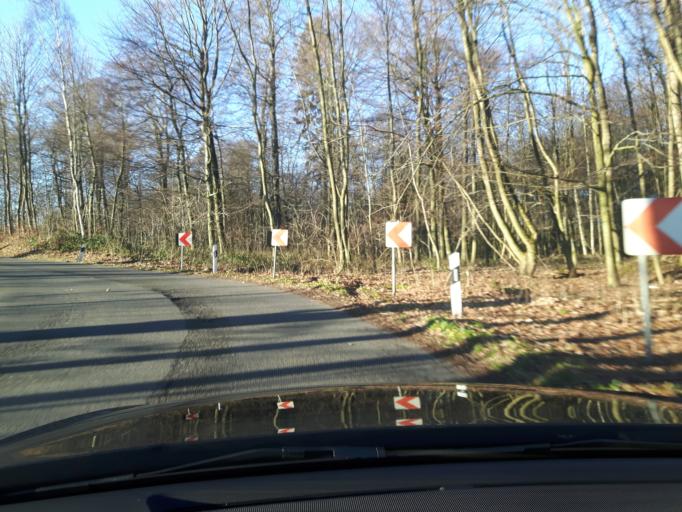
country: DE
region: Mecklenburg-Vorpommern
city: Sehlen
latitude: 54.3810
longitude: 13.4175
